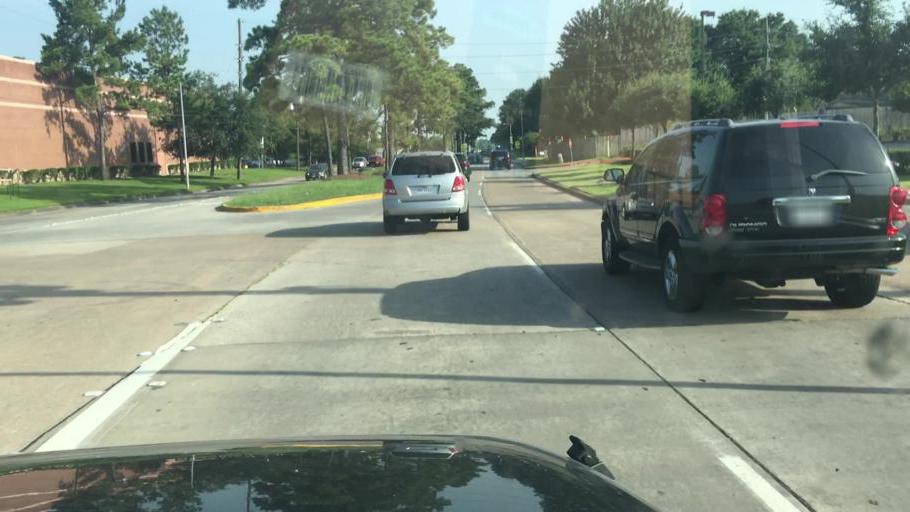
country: US
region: Texas
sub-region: Harris County
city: Atascocita
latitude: 29.9971
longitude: -95.1619
